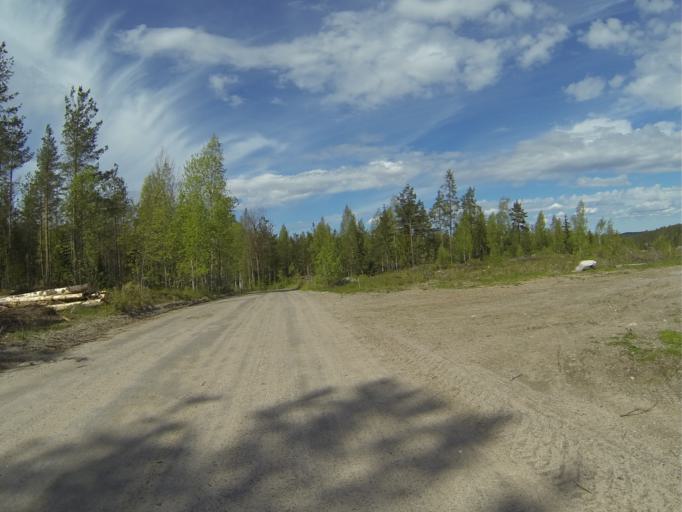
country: FI
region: Varsinais-Suomi
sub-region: Salo
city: Halikko
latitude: 60.3253
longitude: 23.0644
